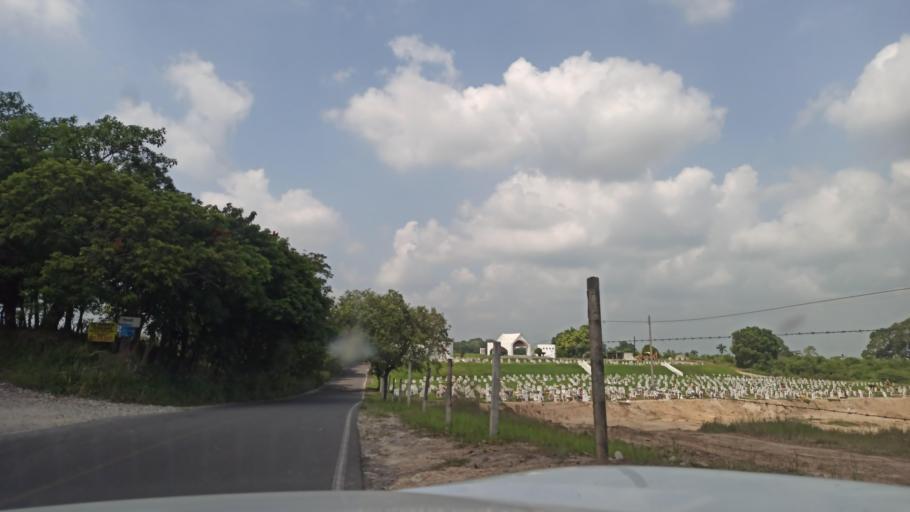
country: MX
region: Veracruz
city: Martinez de la Torre
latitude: 20.0835
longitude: -97.0727
